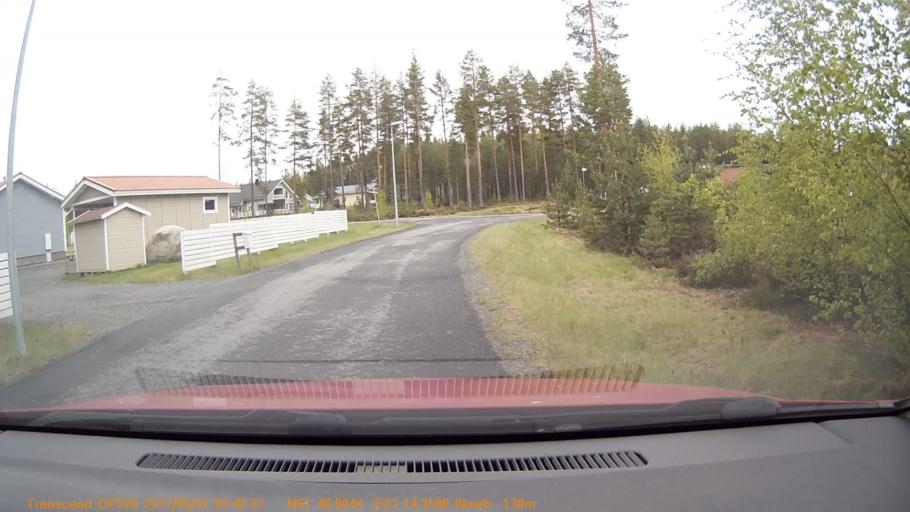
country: FI
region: Pirkanmaa
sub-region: Tampere
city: Viljakkala
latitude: 61.6667
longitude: 23.2393
